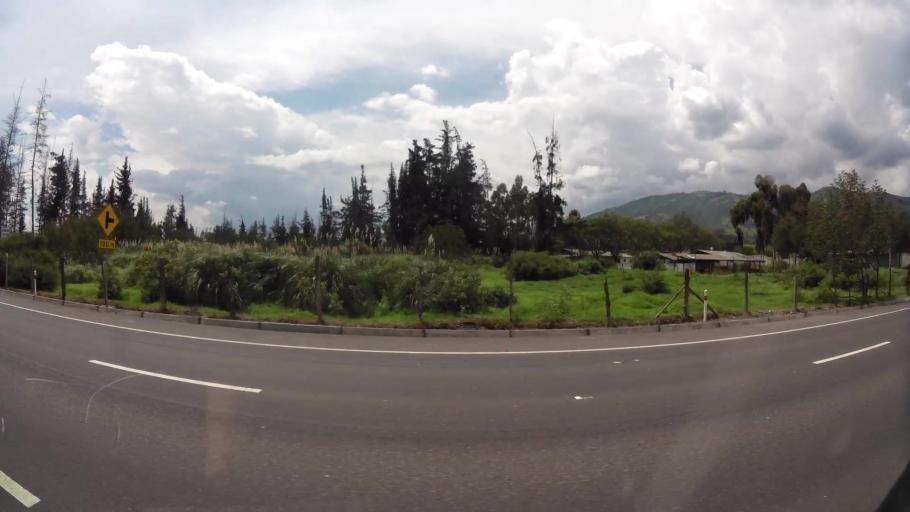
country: EC
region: Pichincha
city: Sangolqui
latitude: -0.2039
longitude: -78.3340
